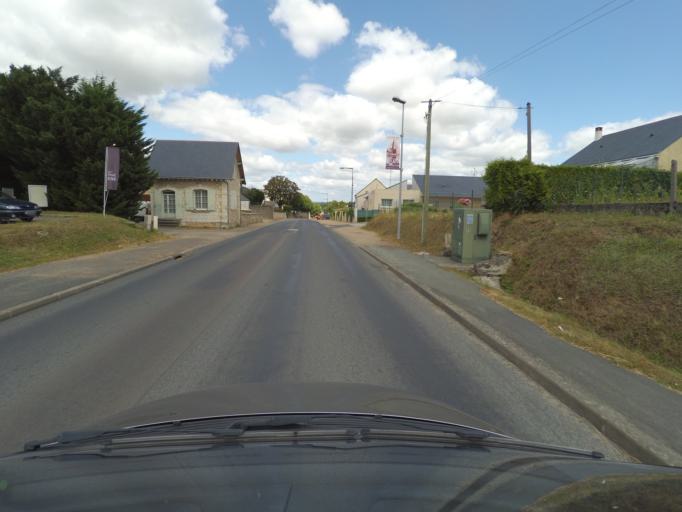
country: FR
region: Pays de la Loire
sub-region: Departement de Maine-et-Loire
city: Gennes
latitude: 47.3358
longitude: -0.2322
